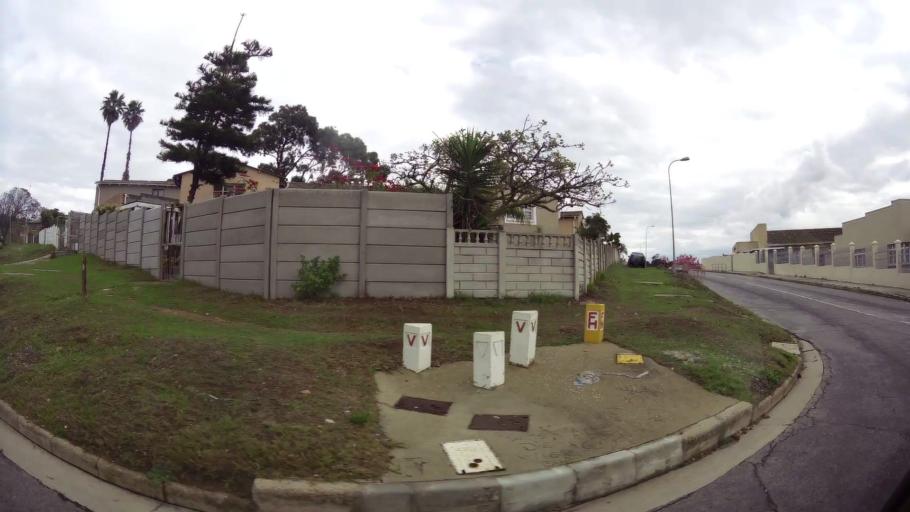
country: ZA
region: Eastern Cape
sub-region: Nelson Mandela Bay Metropolitan Municipality
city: Port Elizabeth
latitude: -33.9422
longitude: 25.5906
